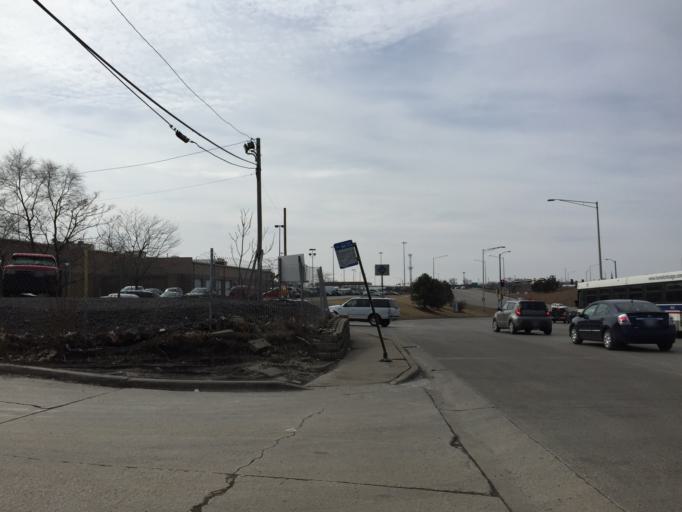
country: US
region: Illinois
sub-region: Cook County
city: Cicero
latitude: 41.8440
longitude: -87.7402
